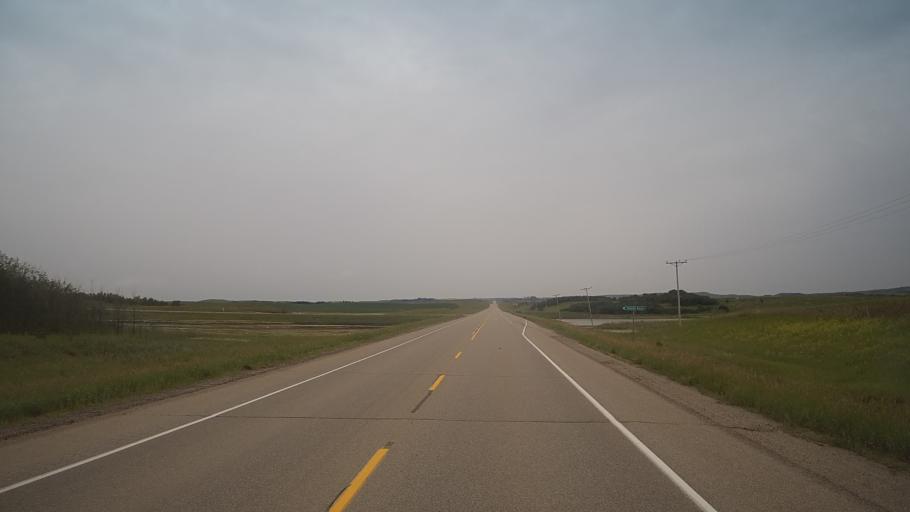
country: CA
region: Saskatchewan
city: Biggar
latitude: 52.0565
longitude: -107.8085
